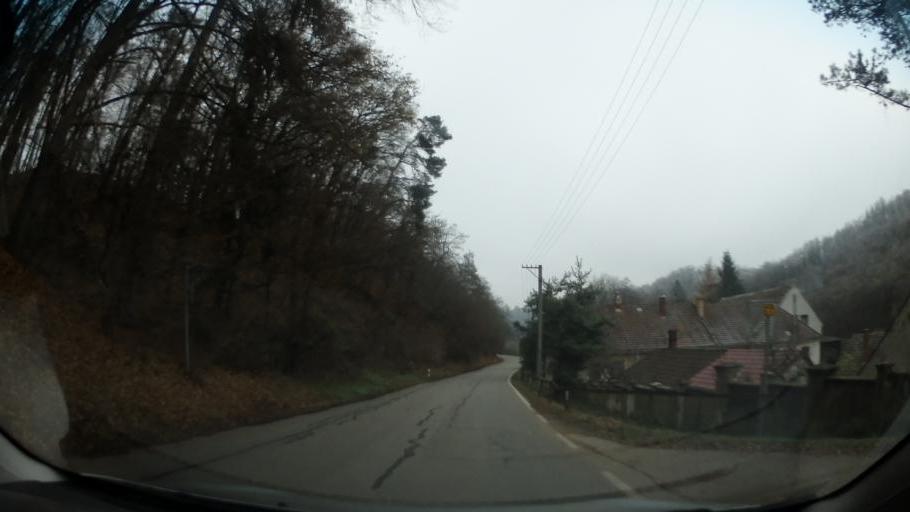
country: CZ
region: Vysocina
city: Mohelno
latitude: 49.1433
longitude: 16.2016
